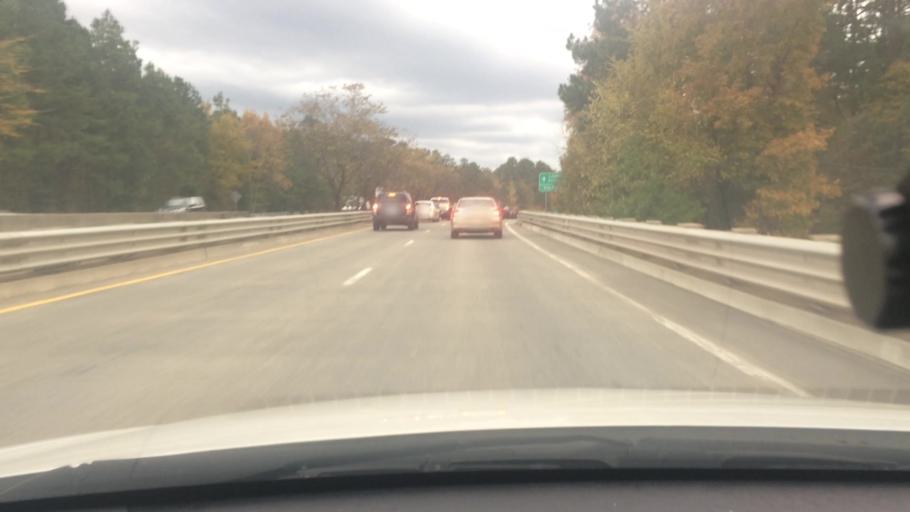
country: US
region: North Carolina
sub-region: Orange County
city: Chapel Hill
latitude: 35.9089
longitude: -79.0272
